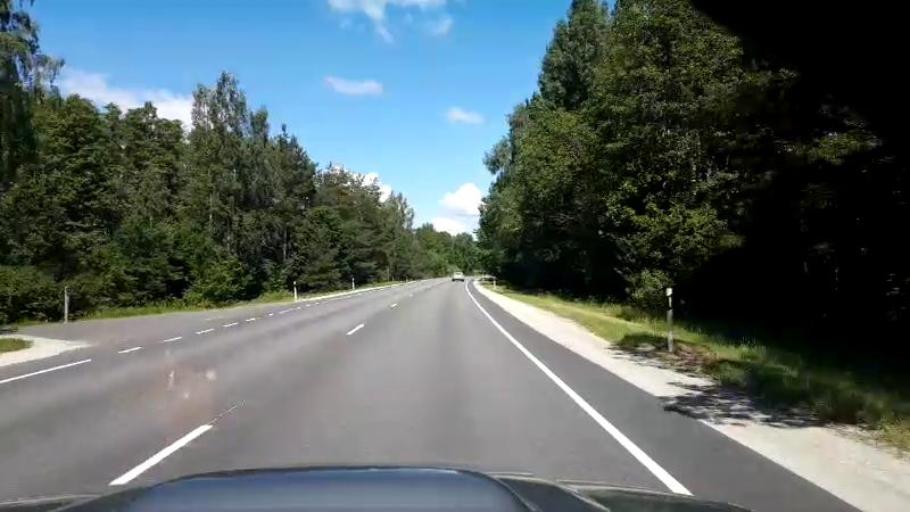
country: EE
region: Paernumaa
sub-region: Paernu linn
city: Parnu
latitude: 58.2171
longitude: 24.4876
